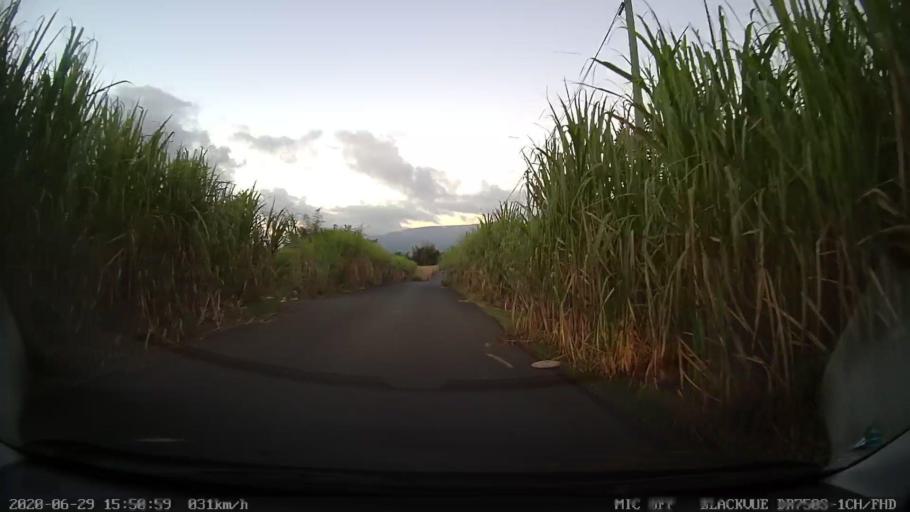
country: RE
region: Reunion
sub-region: Reunion
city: Bras-Panon
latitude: -20.9918
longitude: 55.6932
